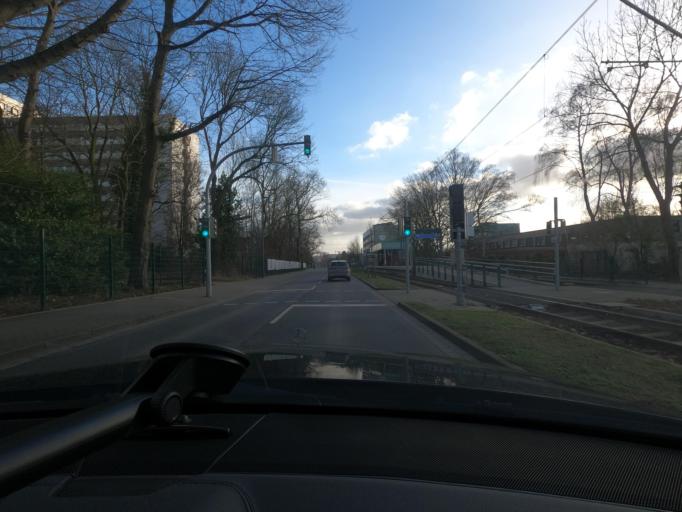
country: DE
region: North Rhine-Westphalia
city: Schwerte
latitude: 51.5069
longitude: 7.5455
